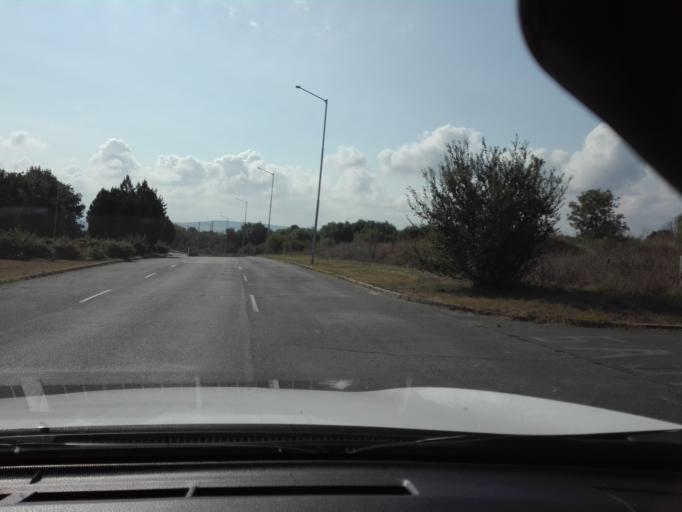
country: BG
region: Burgas
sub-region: Obshtina Burgas
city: Burgas
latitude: 42.4514
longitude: 27.4216
